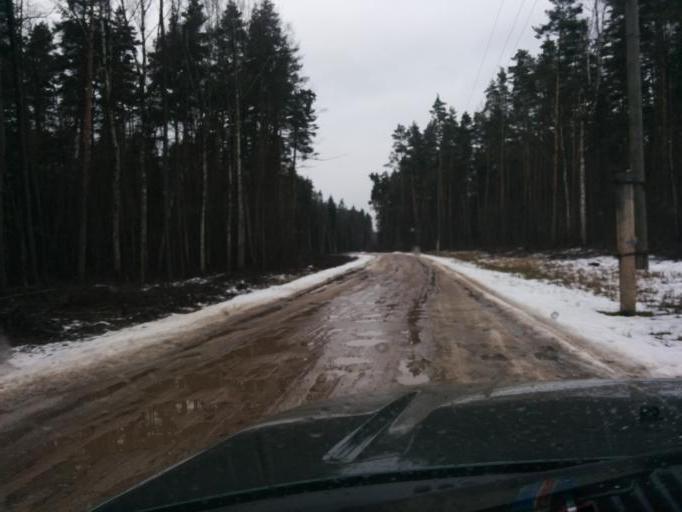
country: LV
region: Ozolnieku
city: Ozolnieki
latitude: 56.6798
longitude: 23.7605
